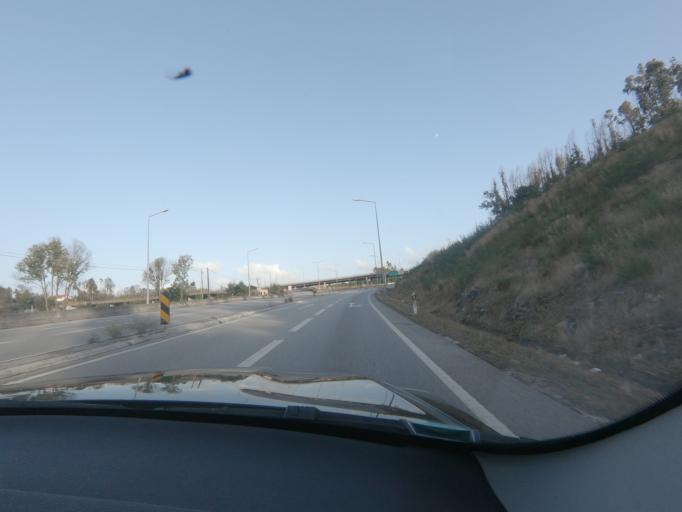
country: PT
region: Viseu
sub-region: Santa Comba Dao
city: Santa Comba Dao
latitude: 40.3848
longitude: -8.1193
